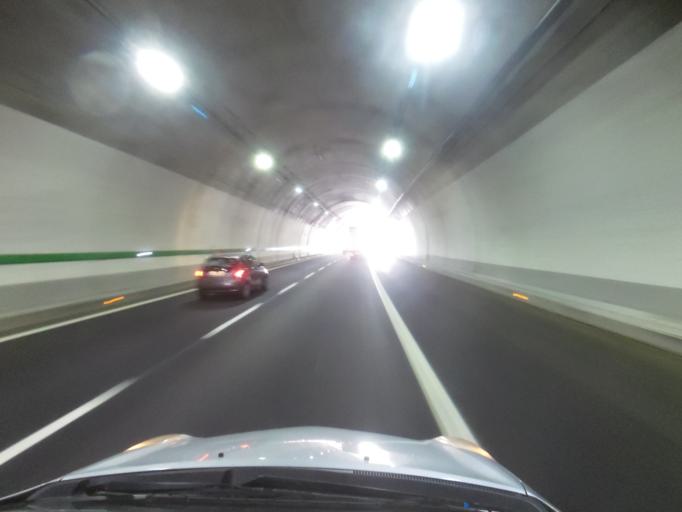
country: IT
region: Tuscany
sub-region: Province of Florence
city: Barberino di Mugello
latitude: 44.0478
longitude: 11.2395
